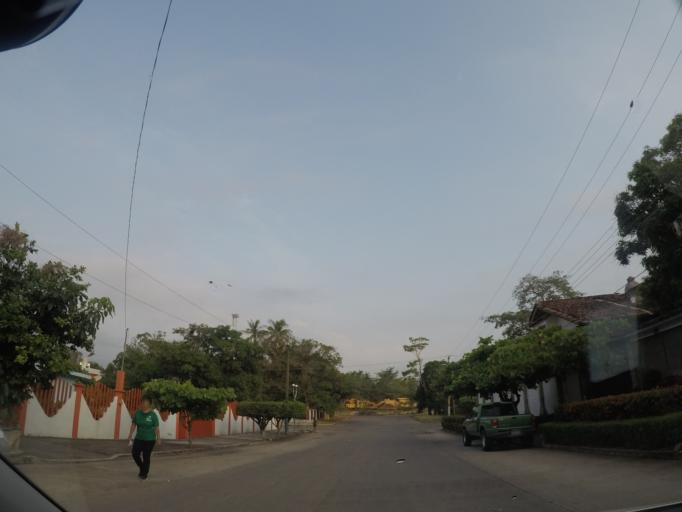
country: MX
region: Oaxaca
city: Matias Romero
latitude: 16.8746
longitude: -95.0439
